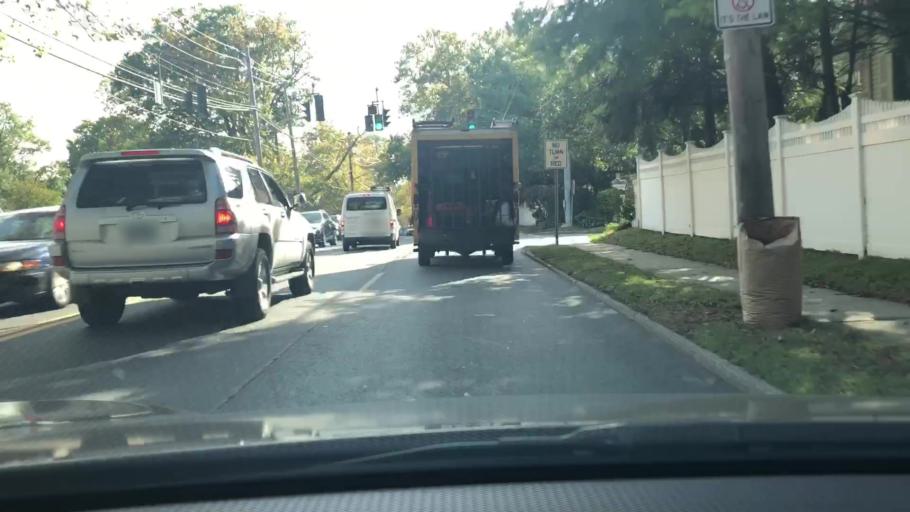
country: US
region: New York
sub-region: Westchester County
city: Tuckahoe
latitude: 40.9618
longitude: -73.8111
